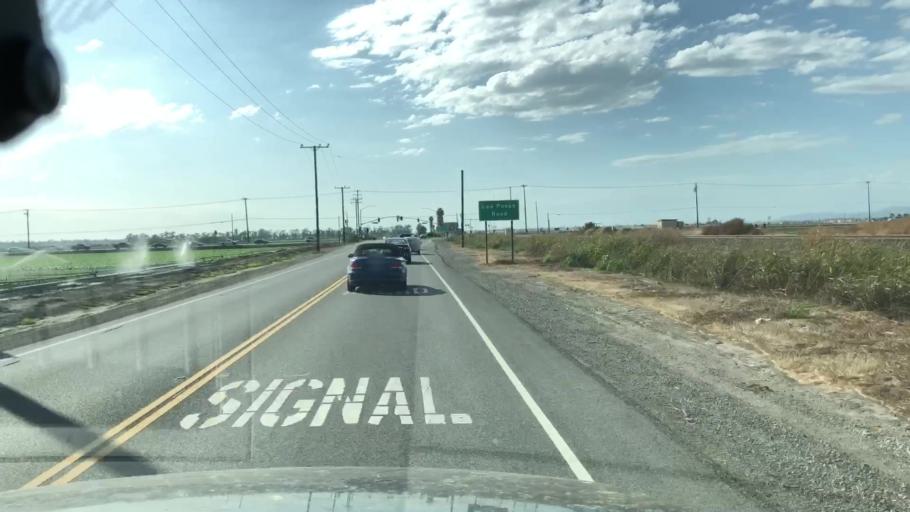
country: US
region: California
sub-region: Ventura County
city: Camarillo
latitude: 34.1964
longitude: -119.0669
